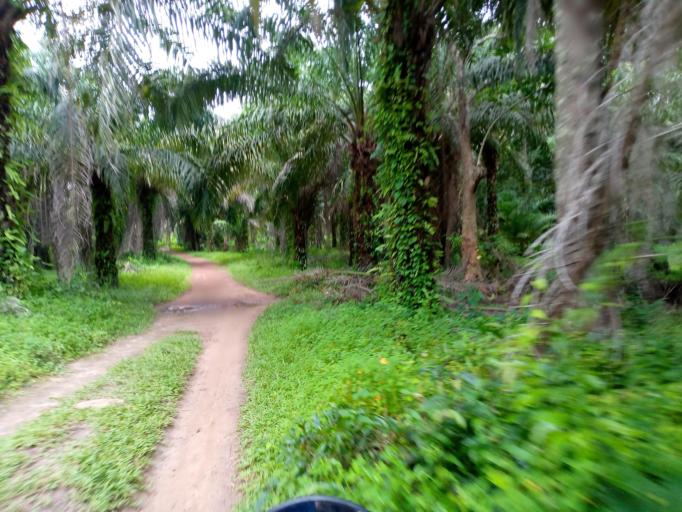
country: SL
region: Northern Province
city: Mange
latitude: 8.9875
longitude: -12.7204
